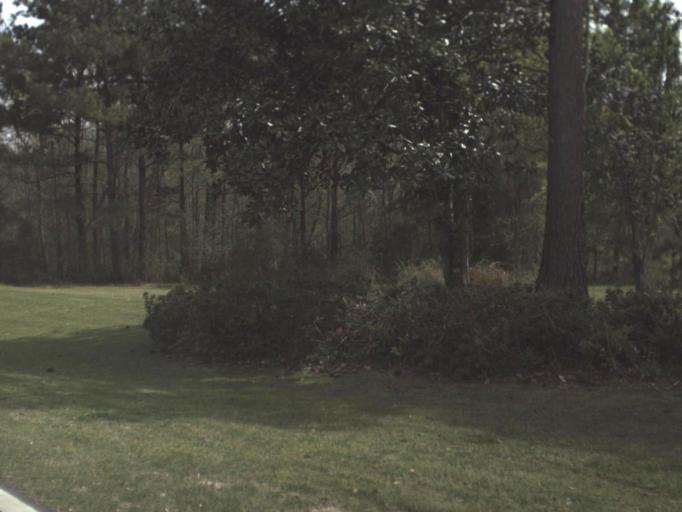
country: US
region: Florida
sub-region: Jackson County
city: Graceville
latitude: 30.9564
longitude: -85.4936
